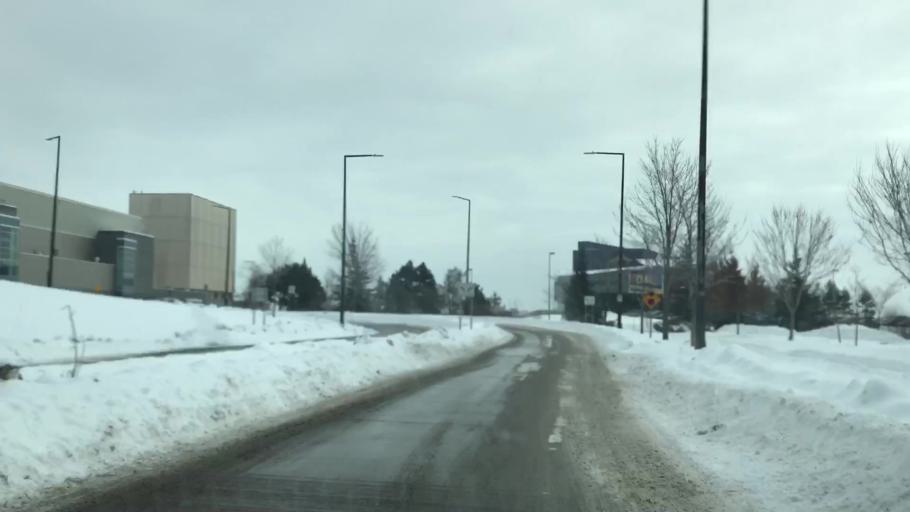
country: US
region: Minnesota
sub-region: Saint Louis County
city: Duluth
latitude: 46.7805
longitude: -92.1020
